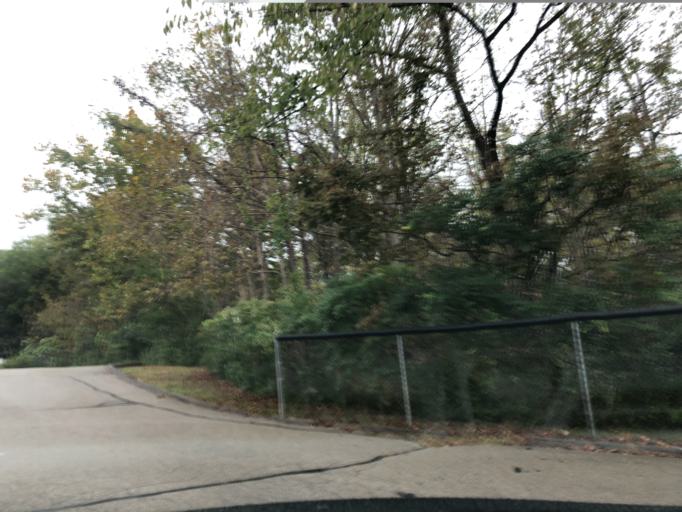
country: US
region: Ohio
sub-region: Hamilton County
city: Loveland
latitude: 39.2598
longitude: -84.2455
